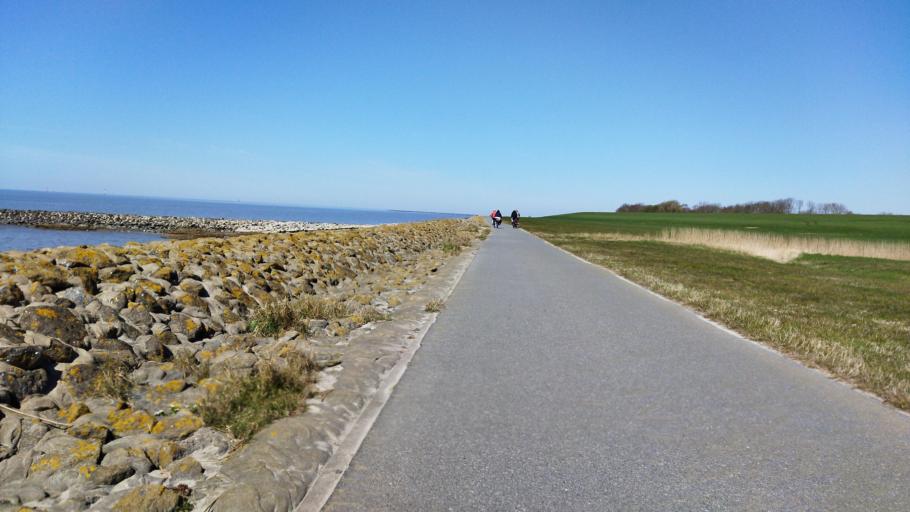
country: DE
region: Lower Saxony
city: Wremen
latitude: 53.6229
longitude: 8.5094
